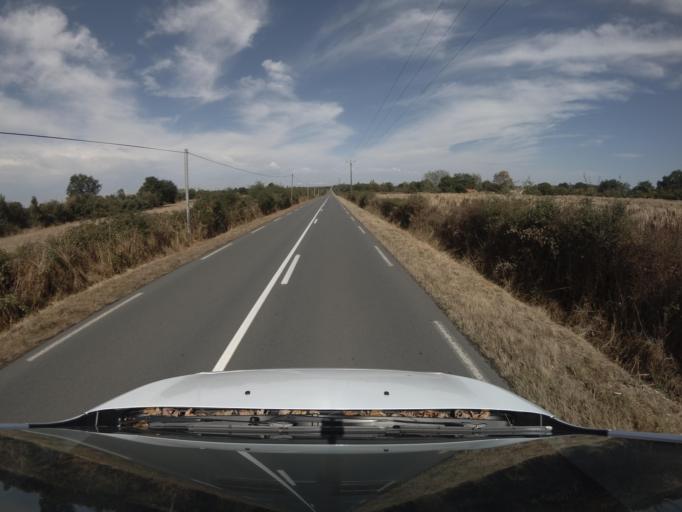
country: FR
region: Poitou-Charentes
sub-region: Departement des Deux-Sevres
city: Nueil-les-Aubiers
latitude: 46.9616
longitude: -0.5758
